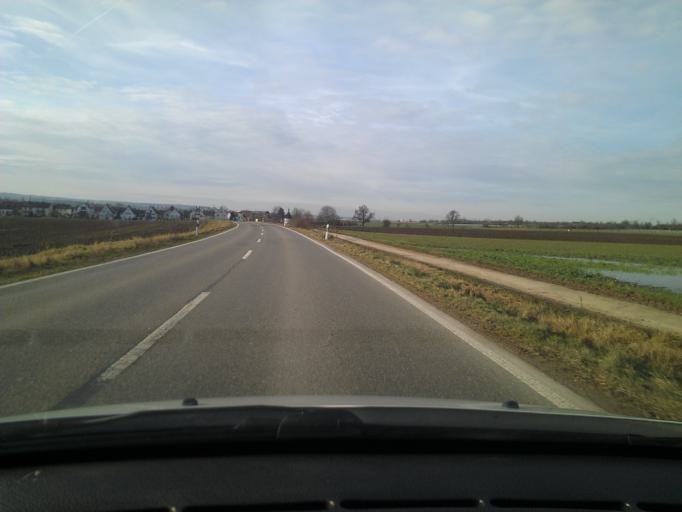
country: DE
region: Baden-Wuerttemberg
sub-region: Regierungsbezirk Stuttgart
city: Neuhausen auf den Fildern
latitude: 48.6900
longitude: 9.2872
